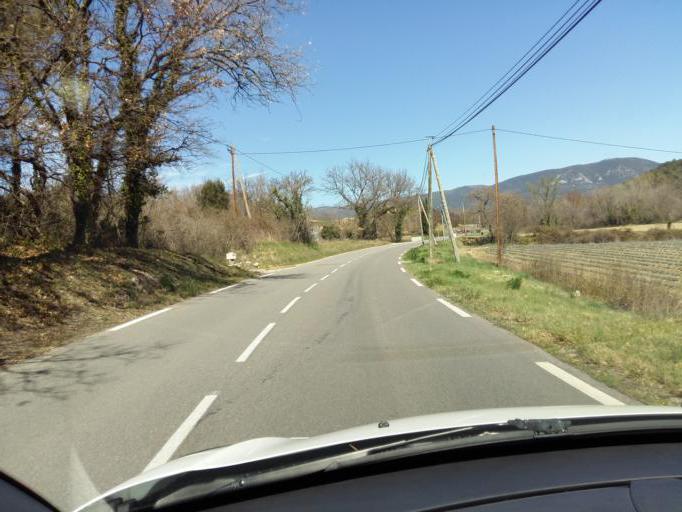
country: FR
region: Provence-Alpes-Cote d'Azur
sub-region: Departement du Vaucluse
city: Apt
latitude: 43.8907
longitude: 5.4276
